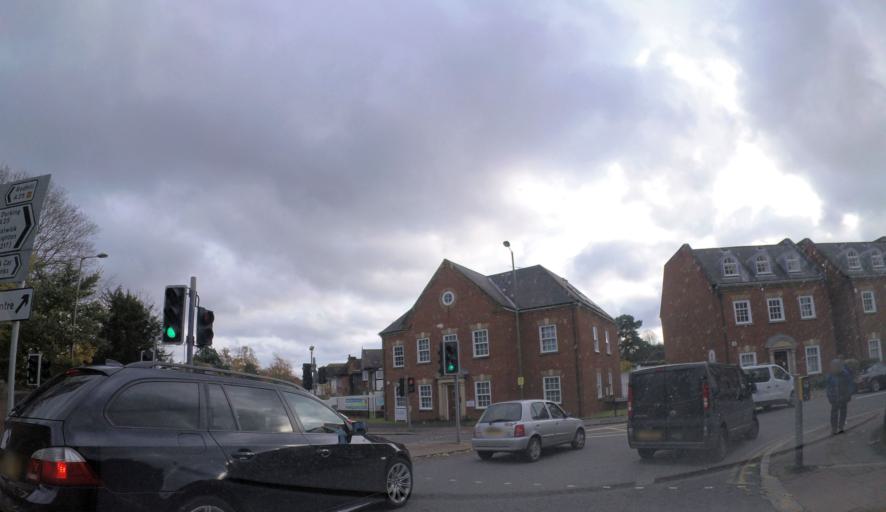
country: GB
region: England
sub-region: Surrey
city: Reigate
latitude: 51.2385
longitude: -0.2024
